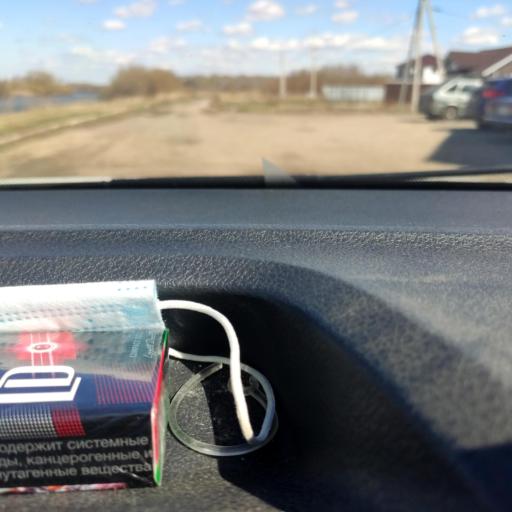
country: RU
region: Bashkortostan
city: Alekseyevka
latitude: 54.6919
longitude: 55.0132
